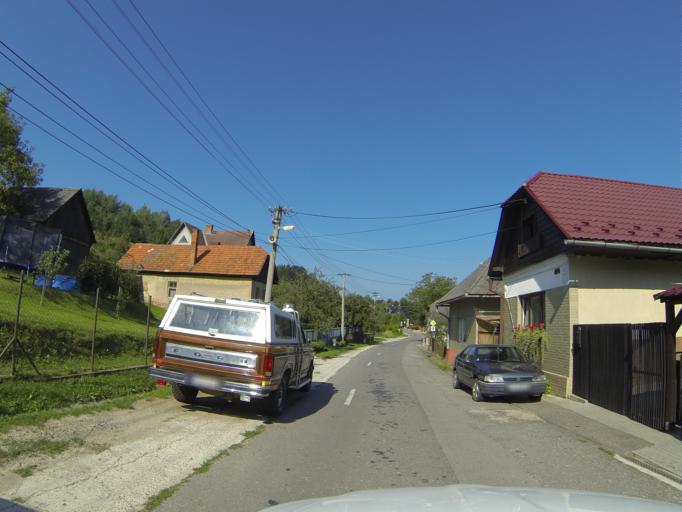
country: SK
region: Nitriansky
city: Handlova
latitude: 48.7750
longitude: 18.7243
